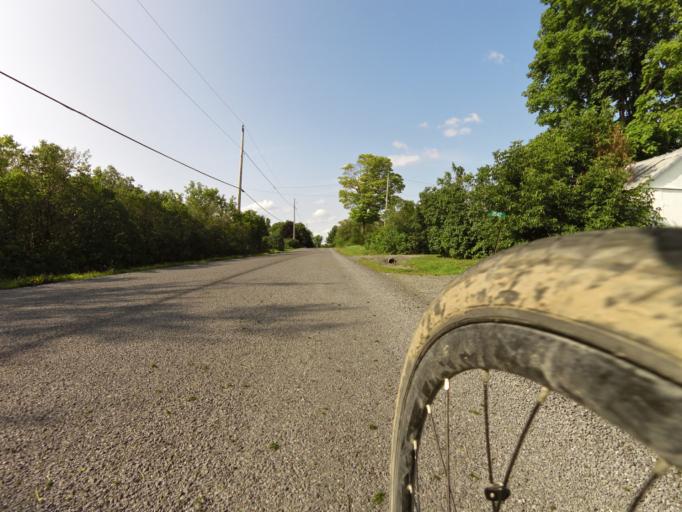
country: CA
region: Ontario
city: Kingston
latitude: 44.3711
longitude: -76.5950
